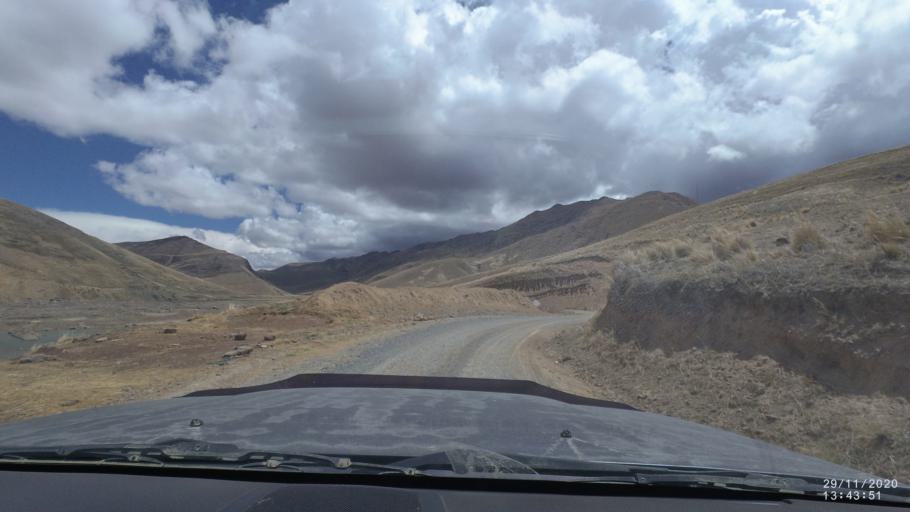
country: BO
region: Cochabamba
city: Cochabamba
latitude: -17.1421
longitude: -66.3186
